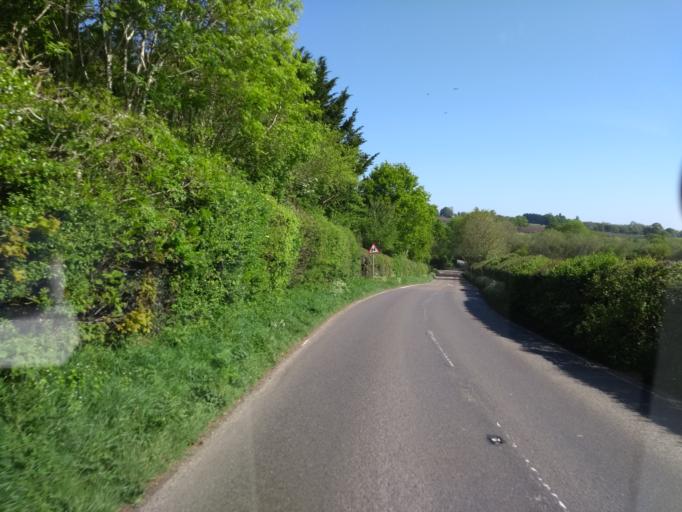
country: GB
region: England
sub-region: Devon
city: Axminster
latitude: 50.8145
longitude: -2.9741
